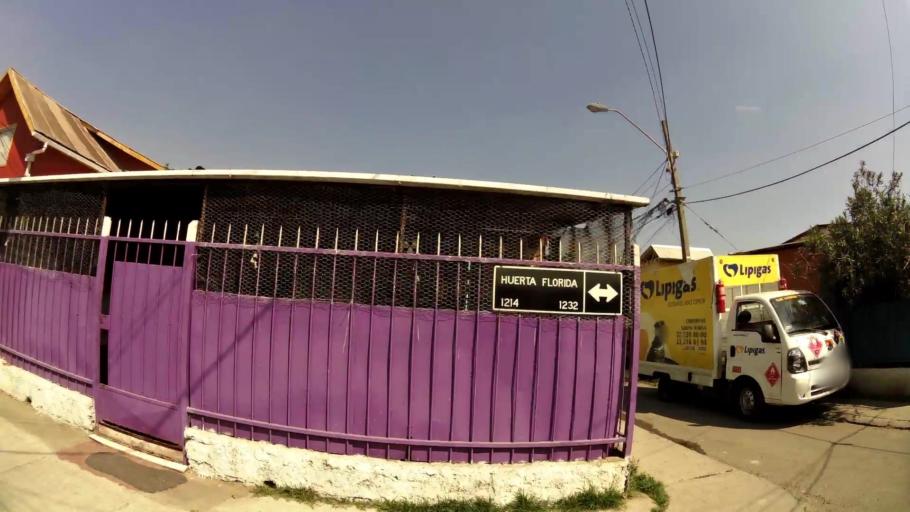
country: CL
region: Santiago Metropolitan
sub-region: Provincia de Santiago
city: La Pintana
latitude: -33.5443
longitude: -70.6026
